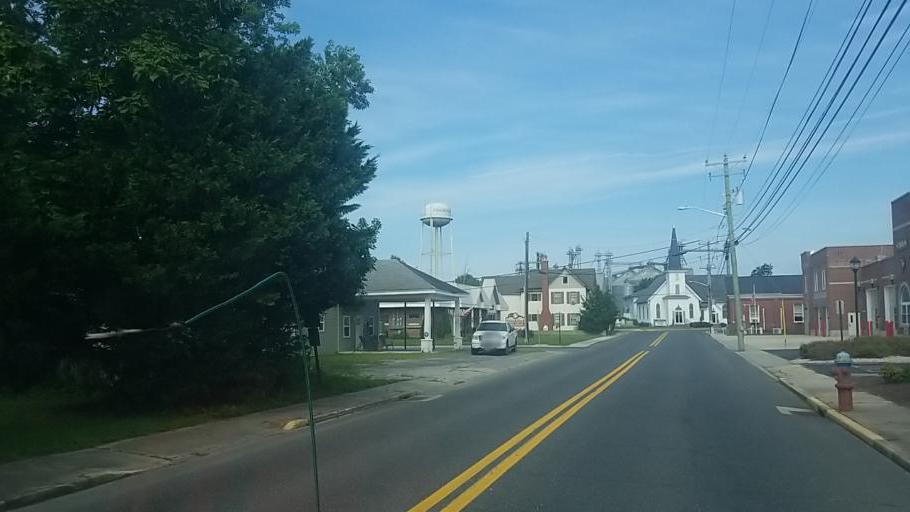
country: US
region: Delaware
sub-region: Sussex County
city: Selbyville
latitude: 38.5172
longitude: -75.2339
